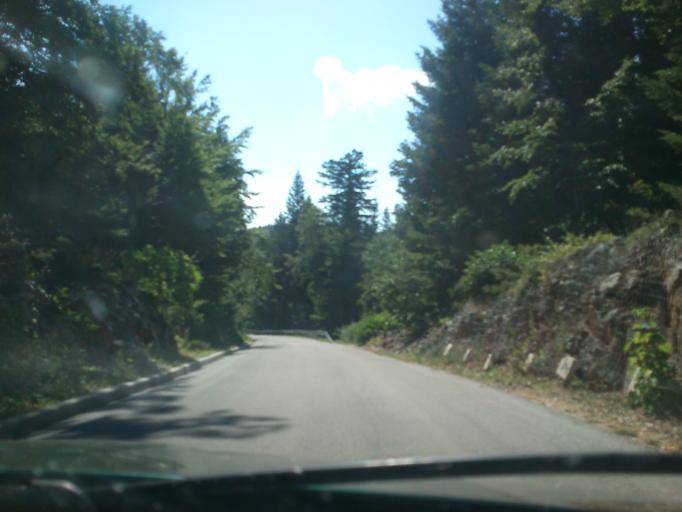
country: HR
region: Licko-Senjska
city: Senj
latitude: 44.8442
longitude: 14.9714
